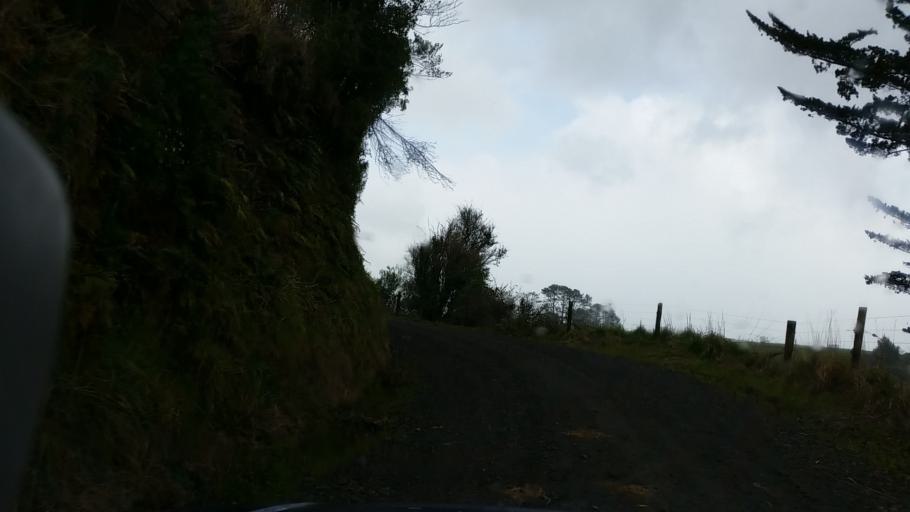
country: NZ
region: Taranaki
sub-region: South Taranaki District
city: Eltham
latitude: -39.2809
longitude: 174.3354
